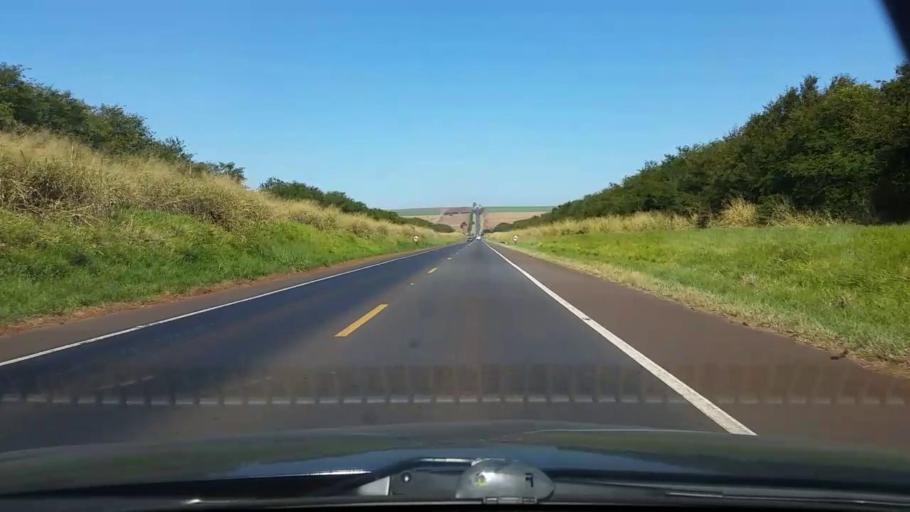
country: BR
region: Sao Paulo
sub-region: Jau
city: Jau
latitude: -22.3632
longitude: -48.5716
